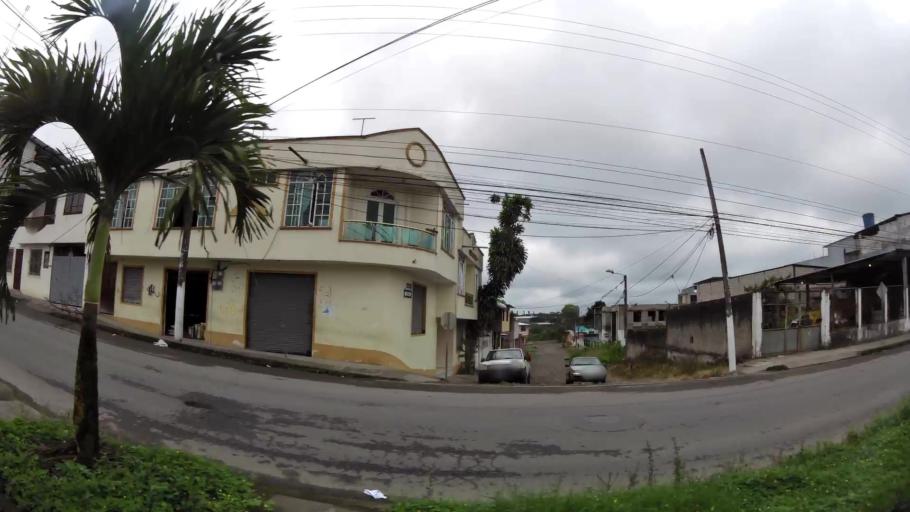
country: EC
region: Santo Domingo de los Tsachilas
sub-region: Canton Santo Domingo de los Colorados
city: Santo Domingo de los Colorados
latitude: -0.2523
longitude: -79.1973
